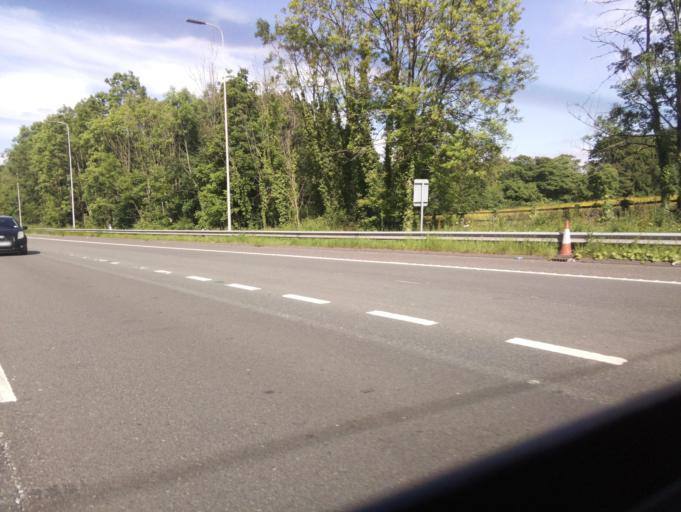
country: GB
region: England
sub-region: City and Borough of Salford
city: Walkden
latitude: 53.5053
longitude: -2.3783
